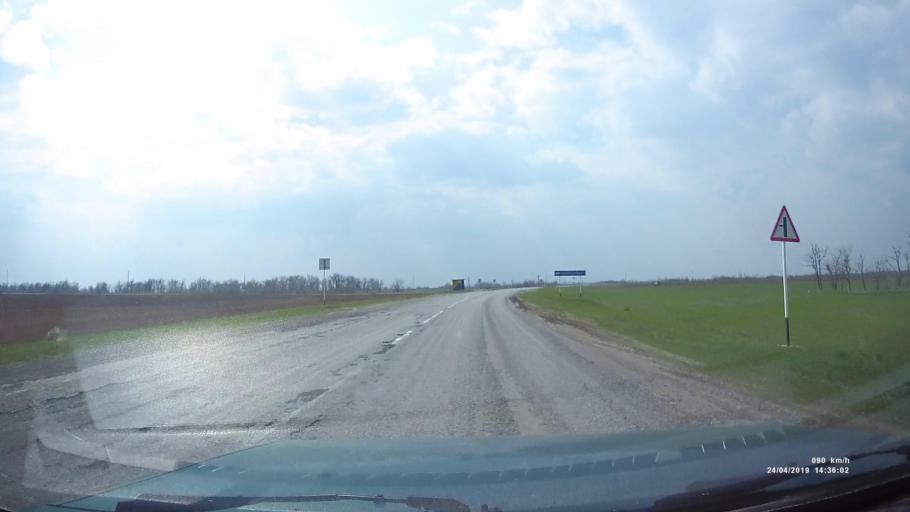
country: RU
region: Rostov
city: Remontnoye
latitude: 46.3754
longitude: 43.8987
